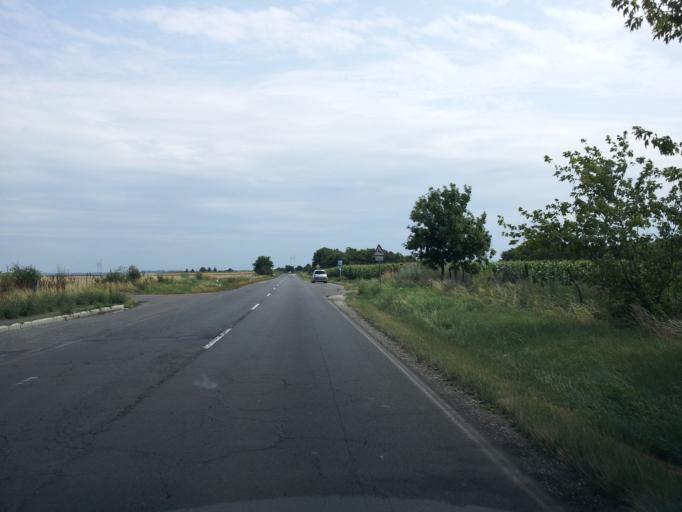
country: HU
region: Fejer
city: Lepseny
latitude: 46.9670
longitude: 18.2088
